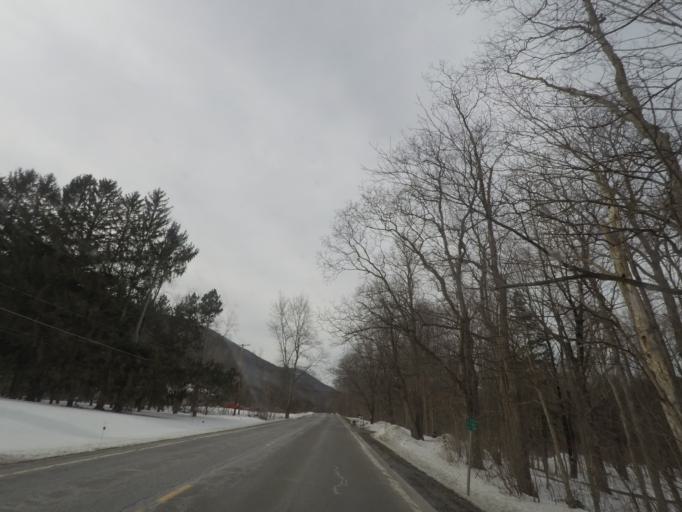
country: US
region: New York
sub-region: Albany County
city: Altamont
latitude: 42.6715
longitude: -74.0093
